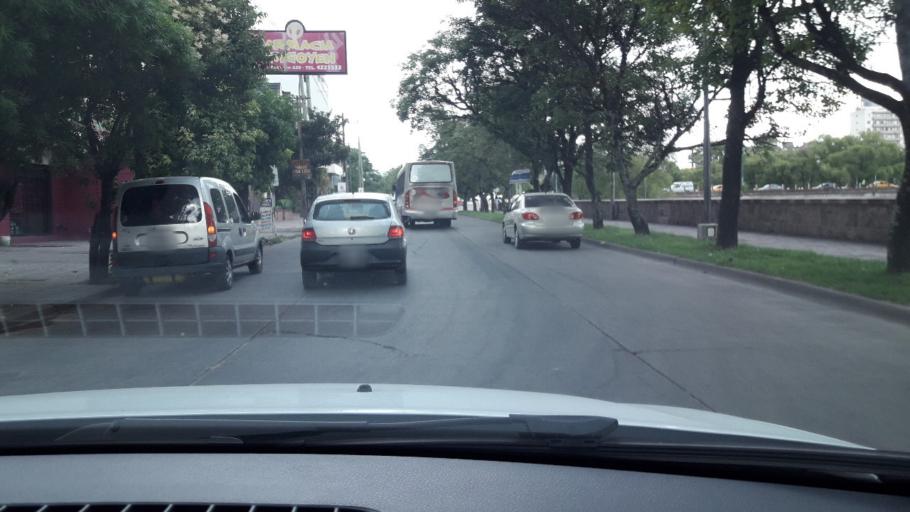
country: AR
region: Jujuy
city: San Salvador de Jujuy
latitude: -24.1901
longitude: -65.2975
